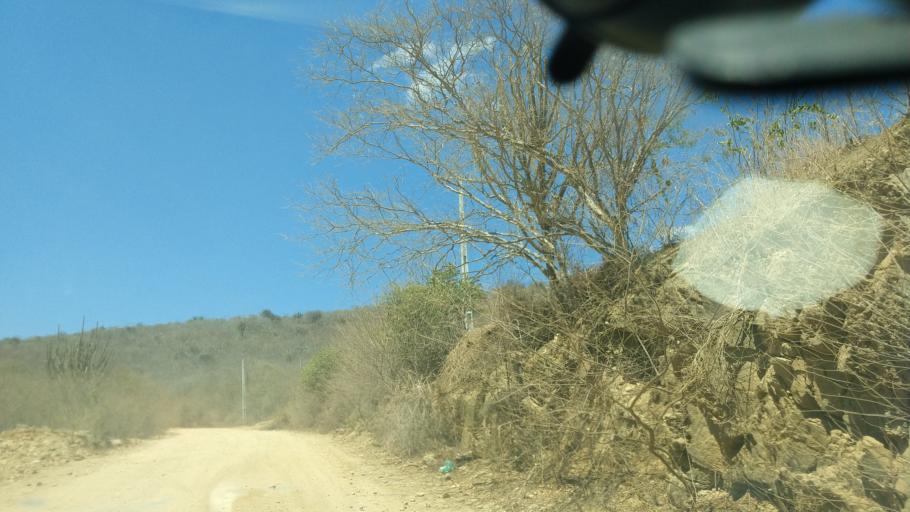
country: BR
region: Rio Grande do Norte
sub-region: Cerro Cora
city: Cerro Cora
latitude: -6.0118
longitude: -36.3169
